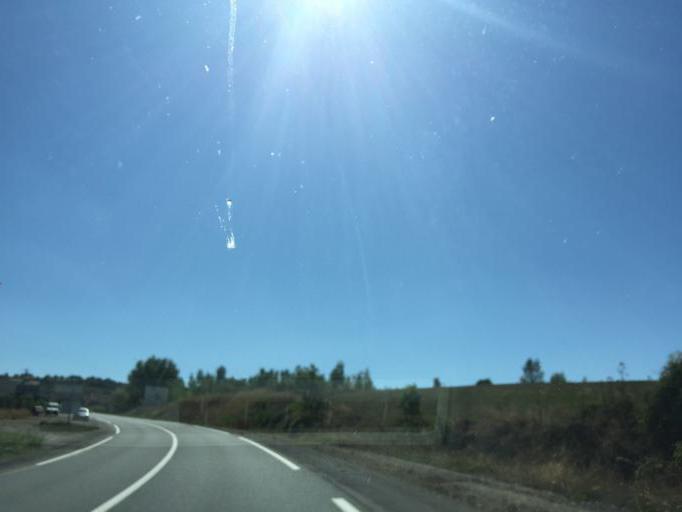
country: FR
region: Midi-Pyrenees
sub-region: Departement de l'Aveyron
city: Saint-Affrique
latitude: 43.9780
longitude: 2.9637
